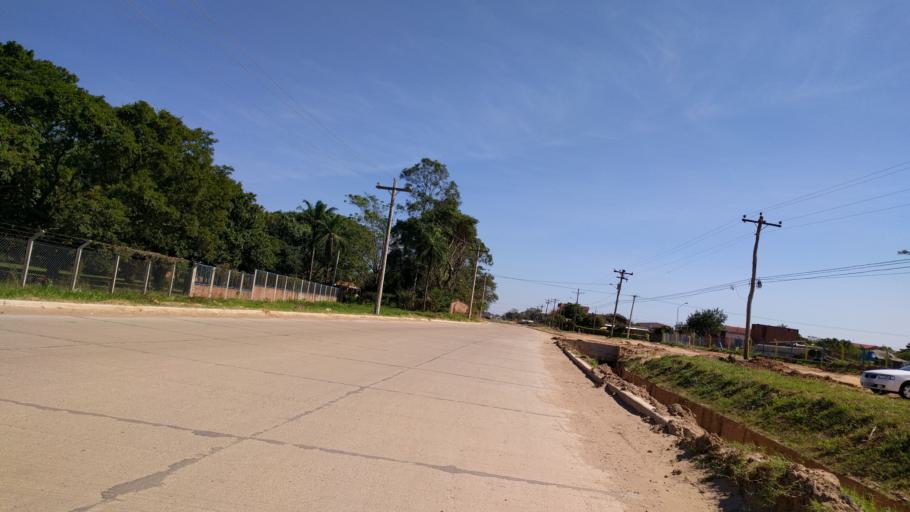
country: BO
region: Santa Cruz
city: Santa Cruz de la Sierra
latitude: -17.8452
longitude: -63.2283
